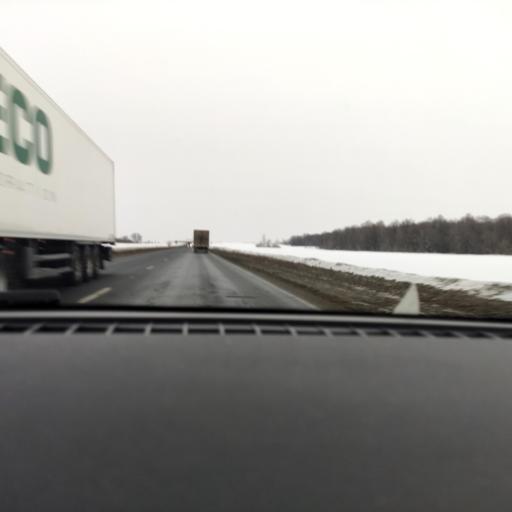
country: RU
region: Samara
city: Petra-Dubrava
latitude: 53.3269
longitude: 50.4543
